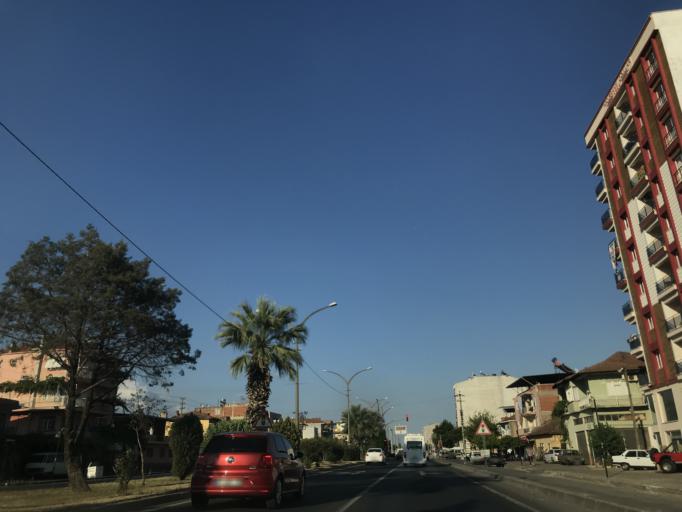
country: TR
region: Aydin
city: Umurlu
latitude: 37.8512
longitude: 27.9635
